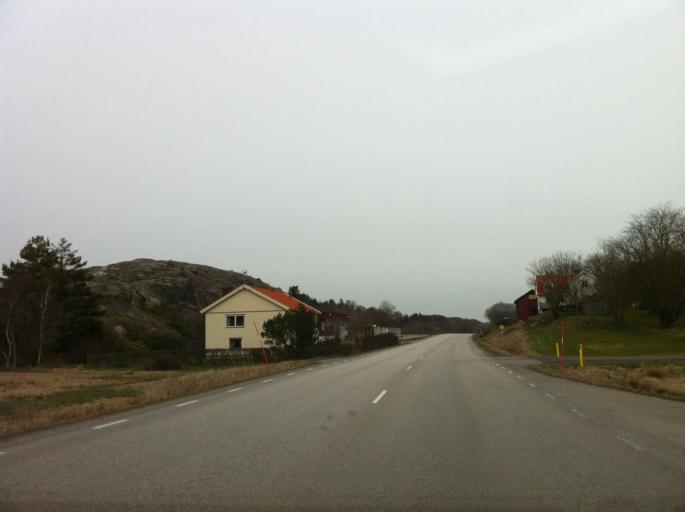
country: SE
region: Vaestra Goetaland
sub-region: Tjorns Kommun
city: Skaerhamn
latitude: 57.9881
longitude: 11.5708
